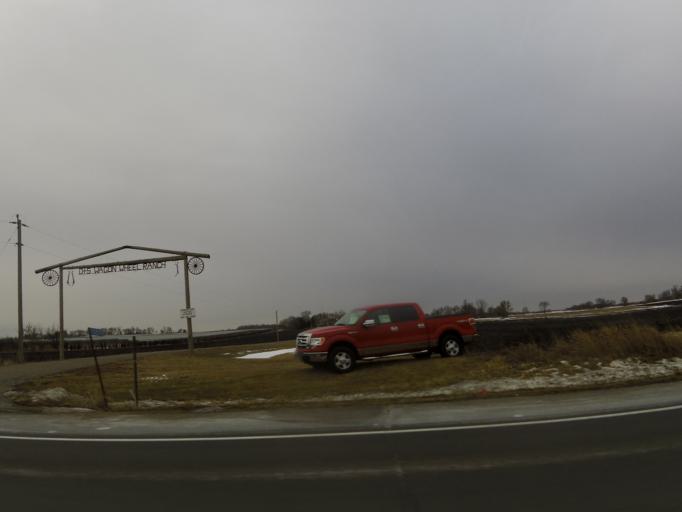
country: US
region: Minnesota
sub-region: Carver County
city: Young America (historical)
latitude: 44.7678
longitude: -93.8598
